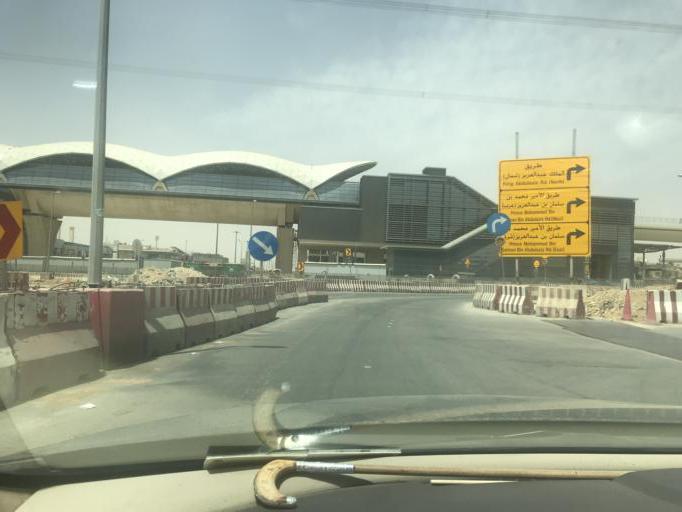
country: SA
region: Ar Riyad
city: Riyadh
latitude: 24.7853
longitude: 46.6608
